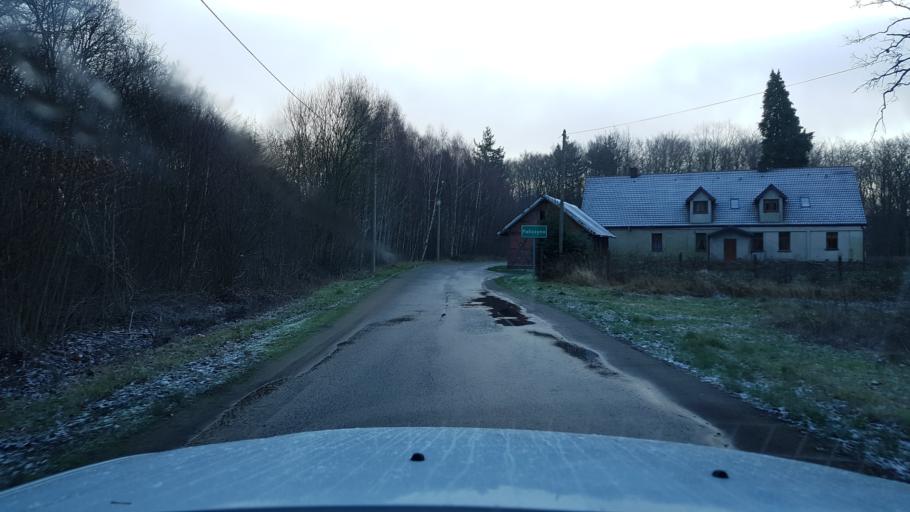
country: PL
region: West Pomeranian Voivodeship
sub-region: Powiat gryficki
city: Trzebiatow
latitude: 54.0480
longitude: 15.3128
